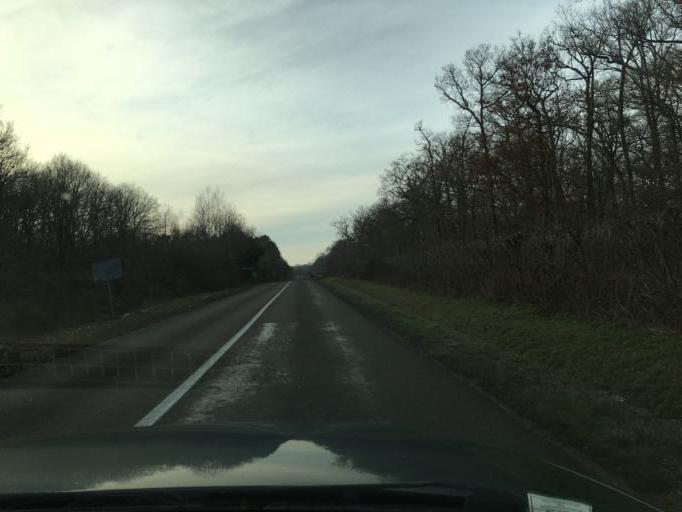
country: FR
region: Centre
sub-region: Departement du Loiret
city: La Ferte-Saint-Aubin
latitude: 47.7304
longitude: 1.9251
